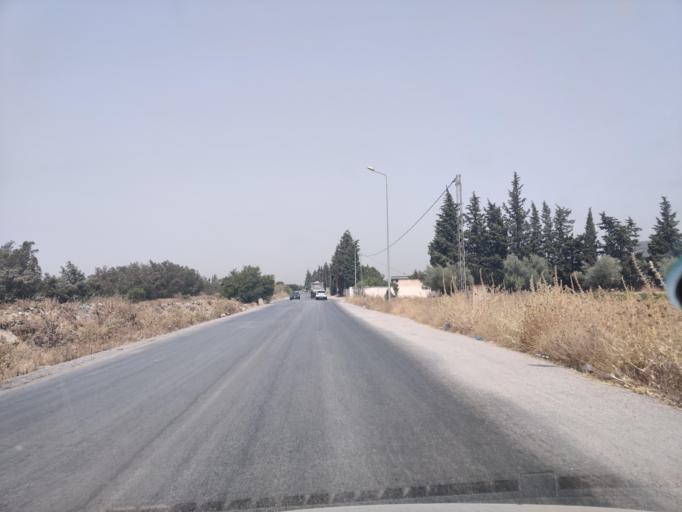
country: TN
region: Tunis
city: La Sebala du Mornag
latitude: 36.6753
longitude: 10.3166
